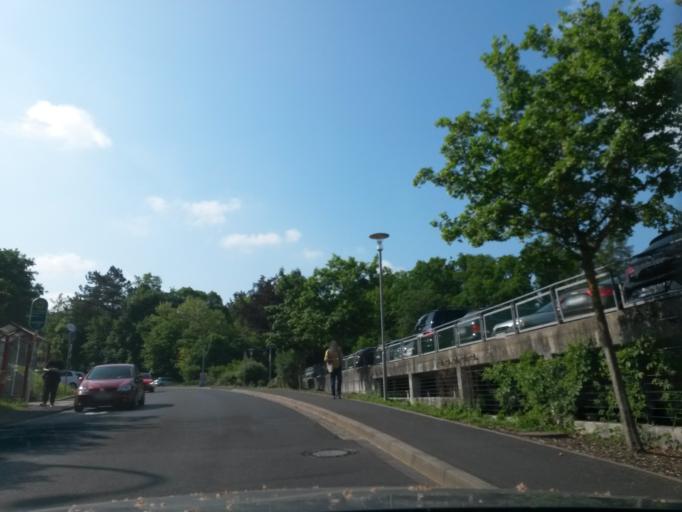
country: DE
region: Bavaria
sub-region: Regierungsbezirk Unterfranken
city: Bad Kissingen
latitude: 50.1895
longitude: 10.0837
